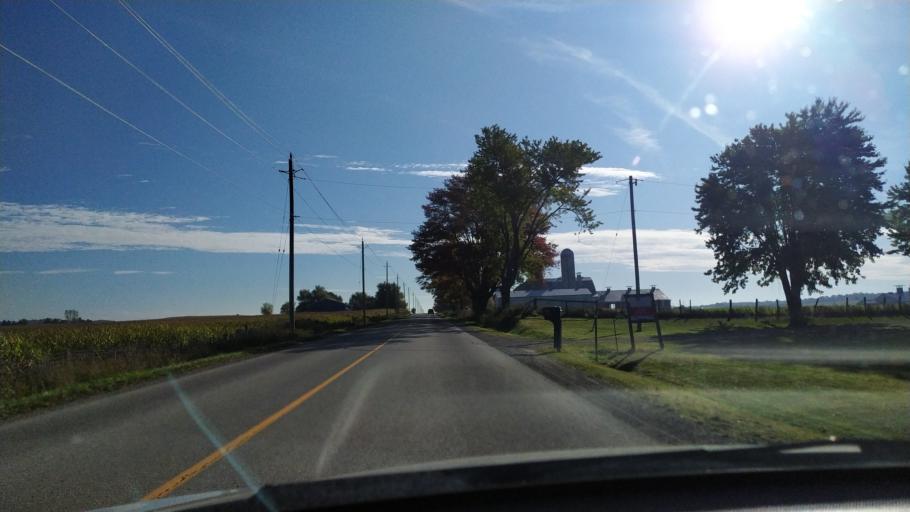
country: CA
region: Ontario
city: Waterloo
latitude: 43.4929
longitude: -80.7294
